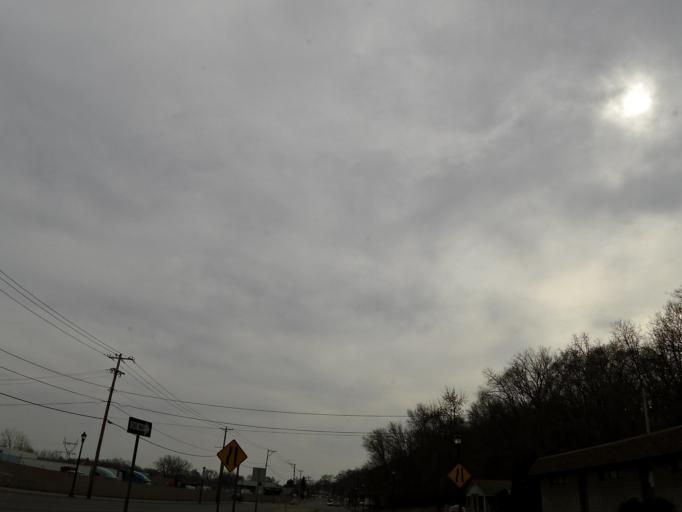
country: US
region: Minnesota
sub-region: Dakota County
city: South Saint Paul
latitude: 44.8726
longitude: -93.0288
